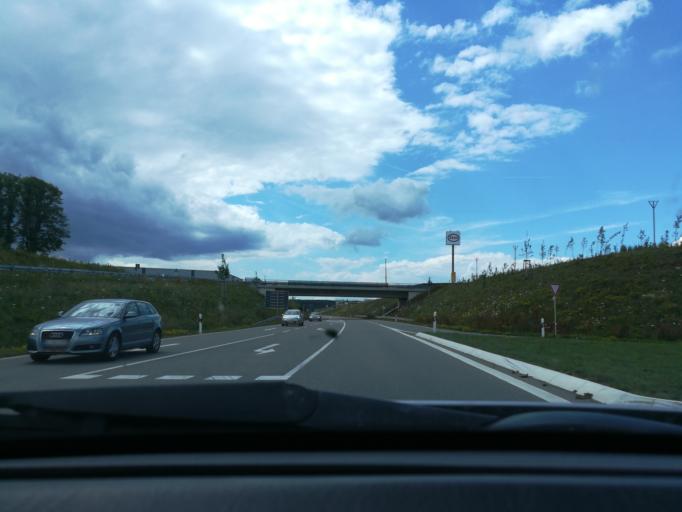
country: DE
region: Baden-Wuerttemberg
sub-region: Freiburg Region
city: Dunningen
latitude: 48.2228
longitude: 8.5029
